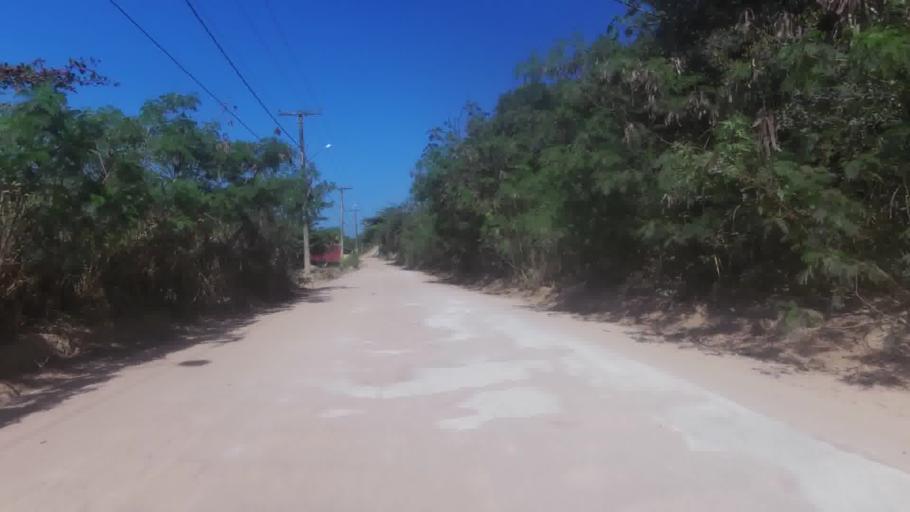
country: BR
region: Espirito Santo
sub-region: Marataizes
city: Marataizes
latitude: -21.0826
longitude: -40.8427
